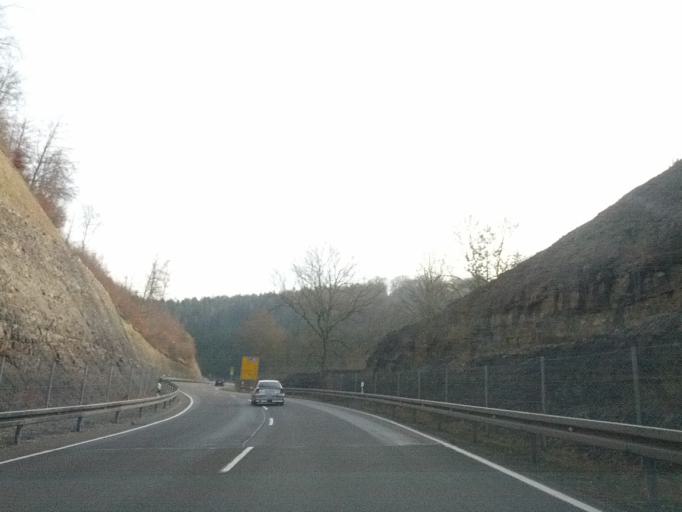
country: DE
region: Thuringia
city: Utendorf
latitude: 50.5860
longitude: 10.4542
